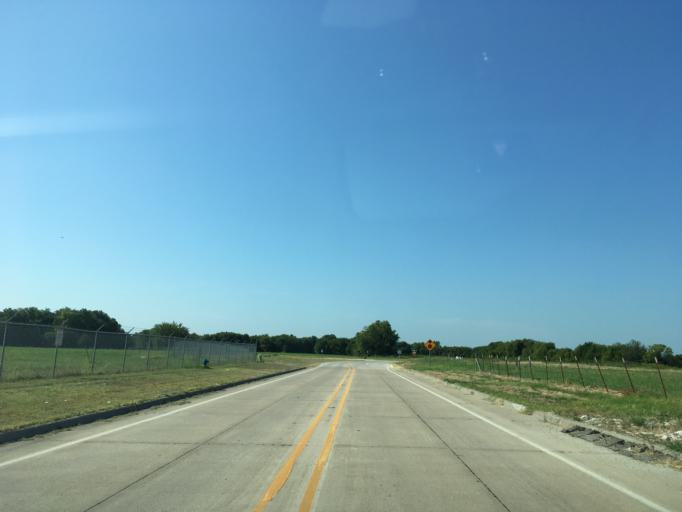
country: US
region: Texas
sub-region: Collin County
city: McKinney
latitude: 33.1671
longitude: -96.5960
